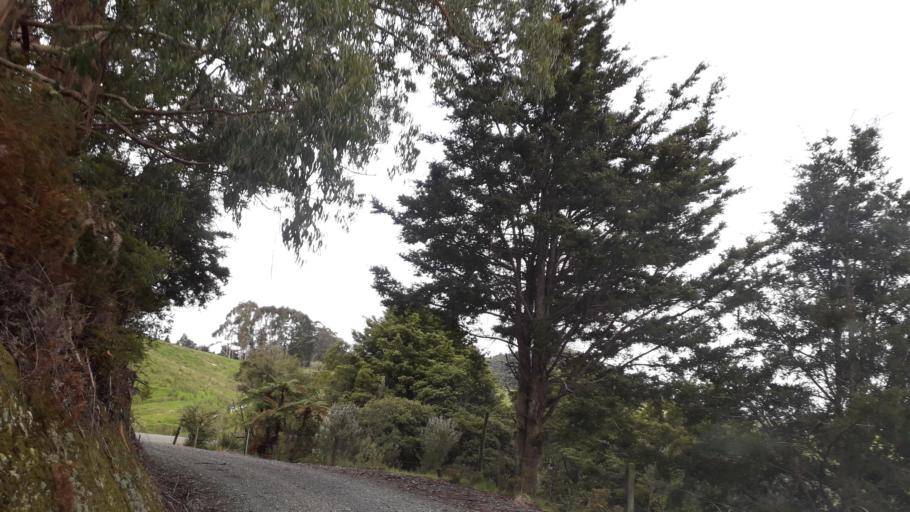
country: NZ
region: Northland
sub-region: Far North District
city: Waimate North
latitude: -35.1601
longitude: 173.7163
